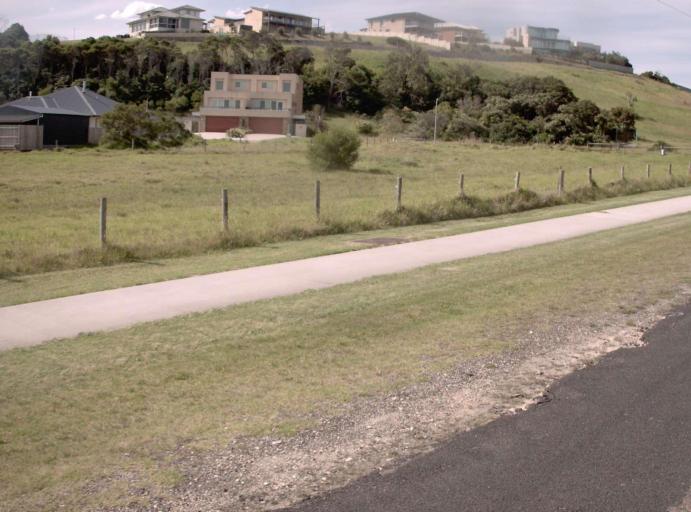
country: AU
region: Victoria
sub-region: East Gippsland
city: Lakes Entrance
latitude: -37.8714
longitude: 148.0108
